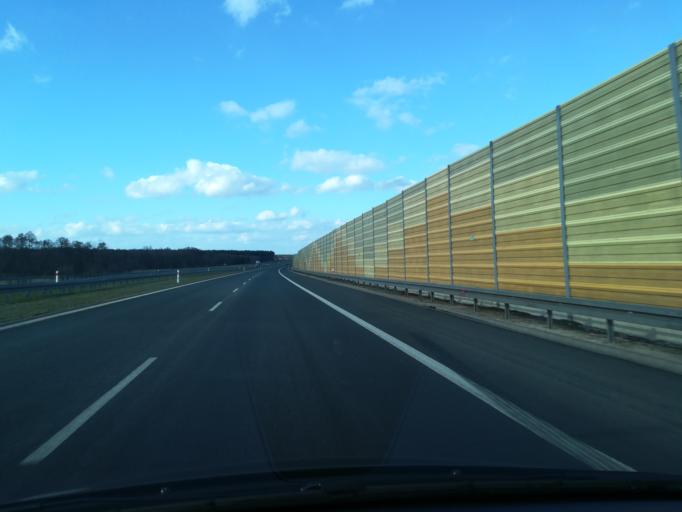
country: PL
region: Lodz Voivodeship
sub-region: Powiat kutnowski
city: Strzelce
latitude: 52.3180
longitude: 19.3621
